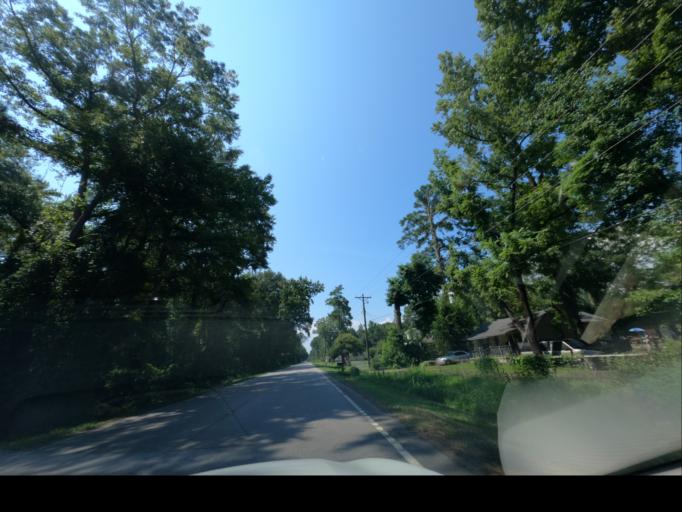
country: US
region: South Carolina
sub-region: Richland County
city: Hopkins
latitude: 33.8948
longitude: -80.9192
